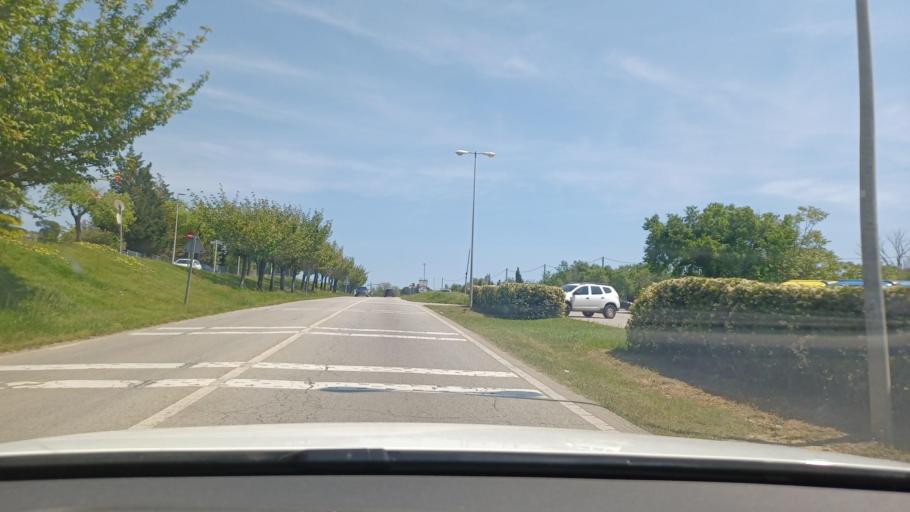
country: ES
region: Catalonia
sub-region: Provincia de Barcelona
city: Rubi
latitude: 41.4808
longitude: 2.0541
